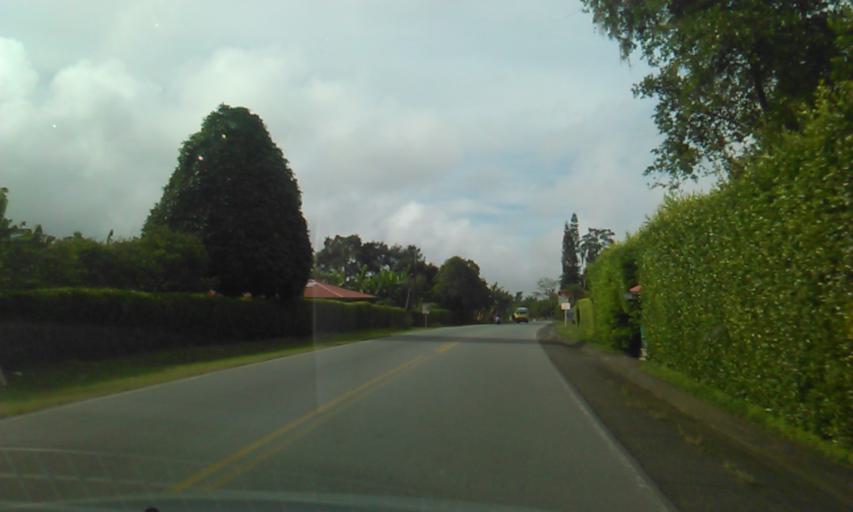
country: CO
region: Quindio
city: Cordoba
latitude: 4.4578
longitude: -75.7114
